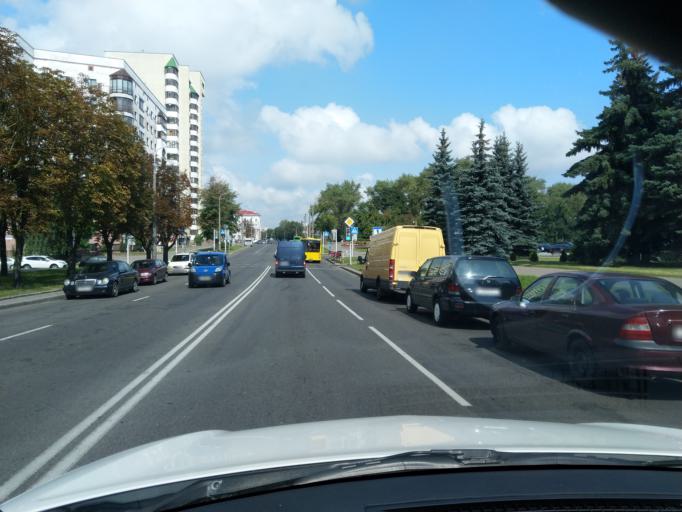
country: BY
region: Minsk
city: Minsk
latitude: 53.9013
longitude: 27.5841
